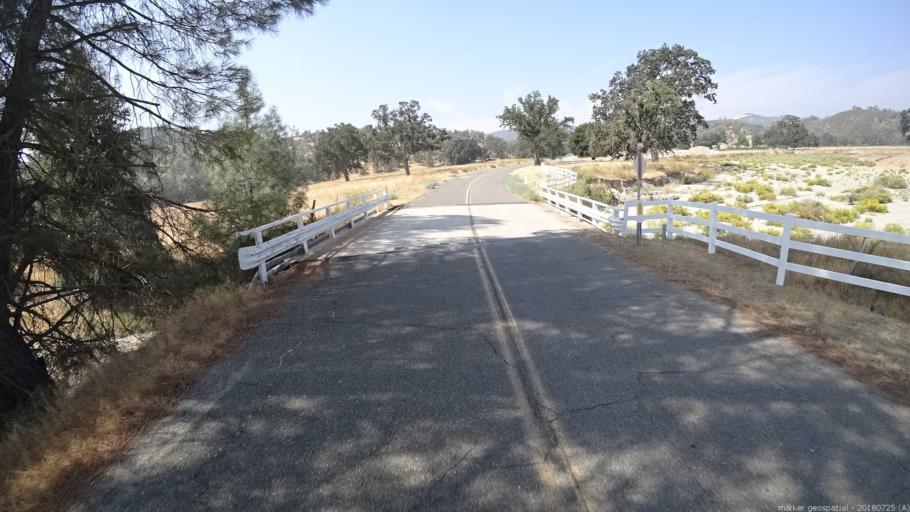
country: US
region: California
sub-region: Fresno County
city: Coalinga
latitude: 35.9262
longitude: -120.5033
